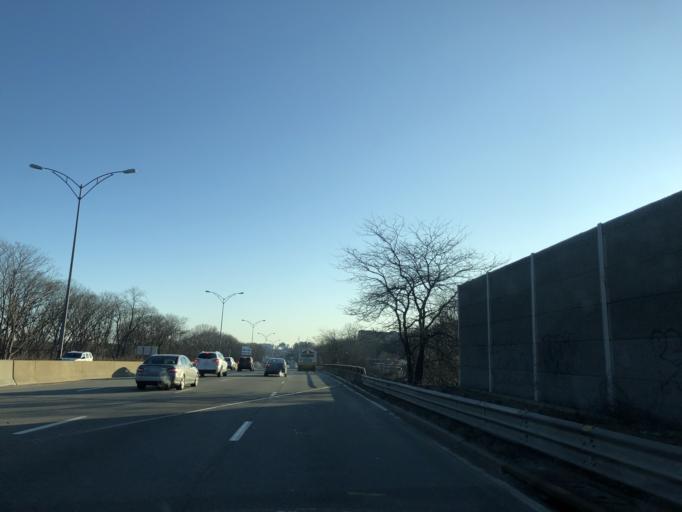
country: US
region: Massachusetts
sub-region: Middlesex County
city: Watertown
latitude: 42.3576
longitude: -71.1737
